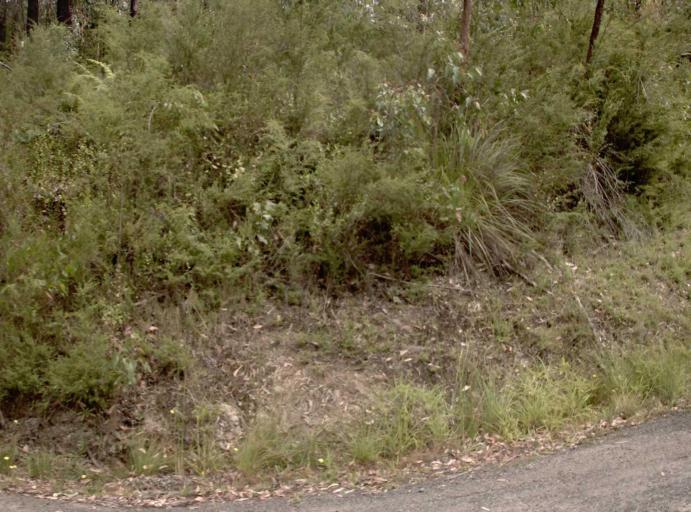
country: AU
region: Victoria
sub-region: Latrobe
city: Morwell
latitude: -38.0653
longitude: 146.4207
